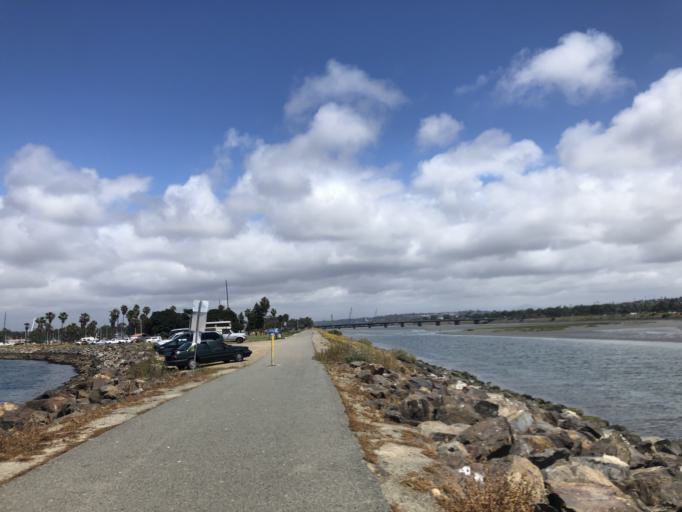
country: US
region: California
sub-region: San Diego County
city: Coronado
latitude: 32.7574
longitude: -117.2447
